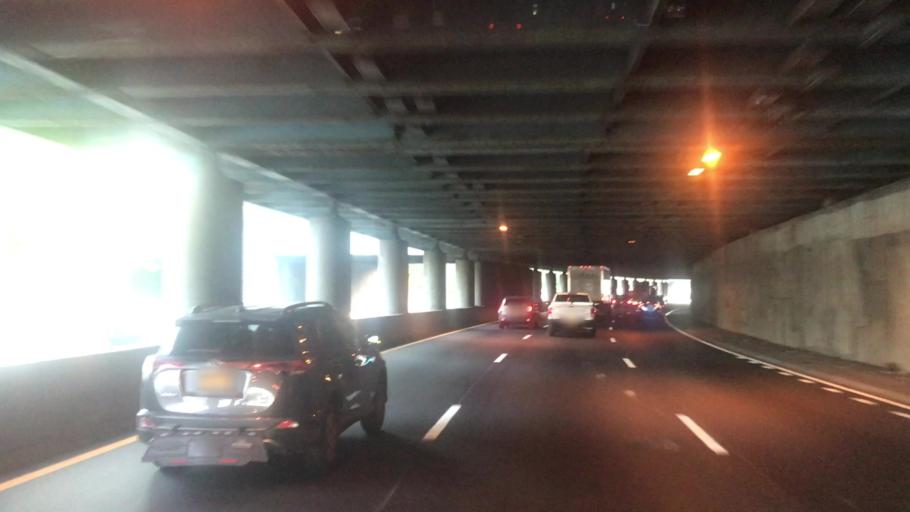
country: US
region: New York
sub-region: New York County
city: Inwood
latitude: 40.8780
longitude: -73.9040
